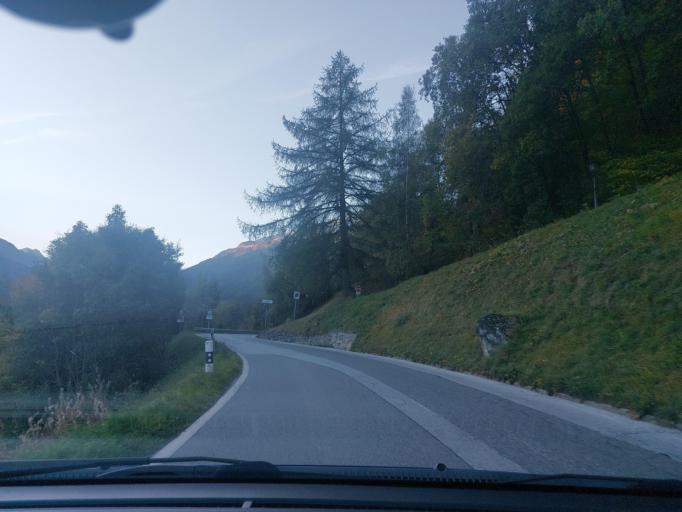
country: CH
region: Valais
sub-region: Sierre District
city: Chippis
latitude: 46.1953
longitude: 7.5840
